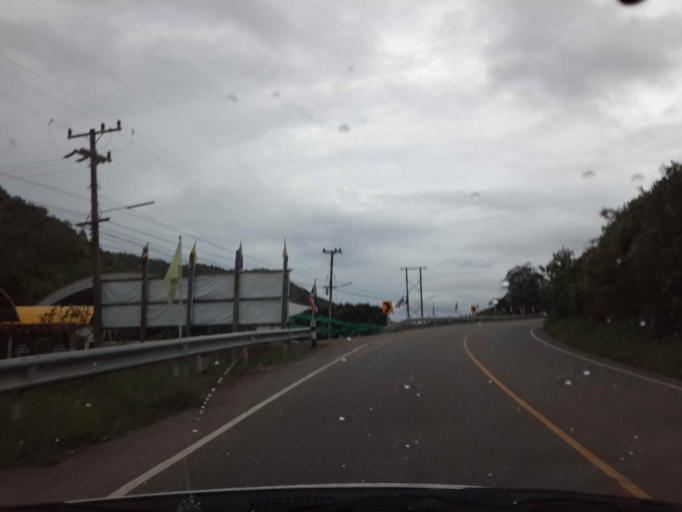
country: TH
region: Ratchaburi
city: Suan Phueng
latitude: 13.5668
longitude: 99.2621
